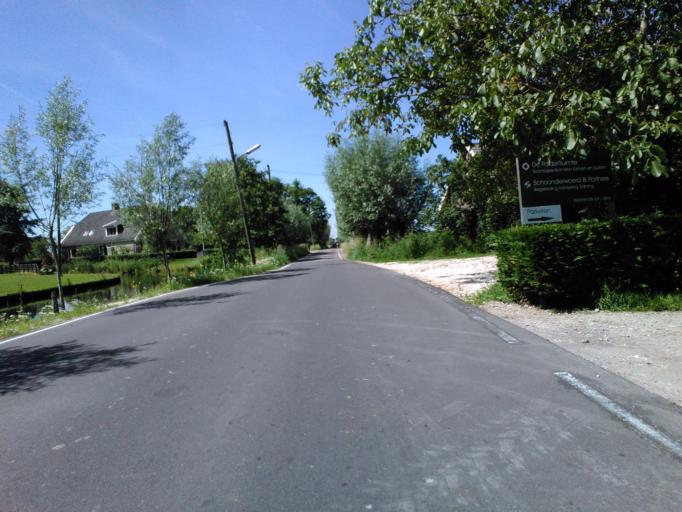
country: NL
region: South Holland
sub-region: Molenwaard
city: Nieuw-Lekkerland
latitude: 51.9388
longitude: 4.6955
